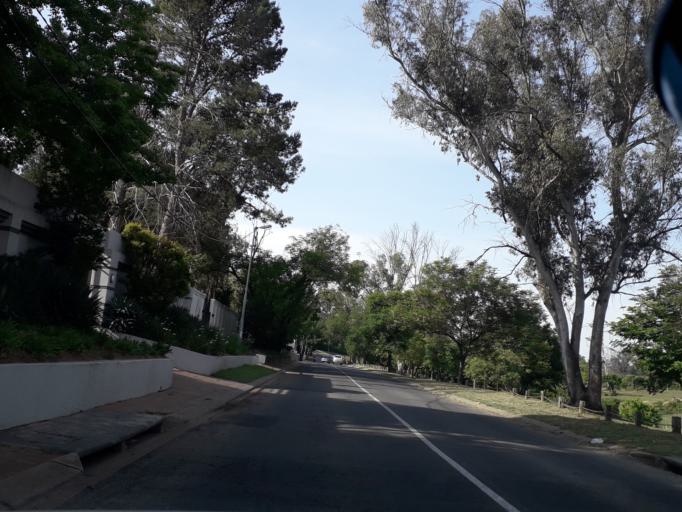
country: ZA
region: Gauteng
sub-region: City of Johannesburg Metropolitan Municipality
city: Midrand
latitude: -26.0651
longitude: 28.0412
